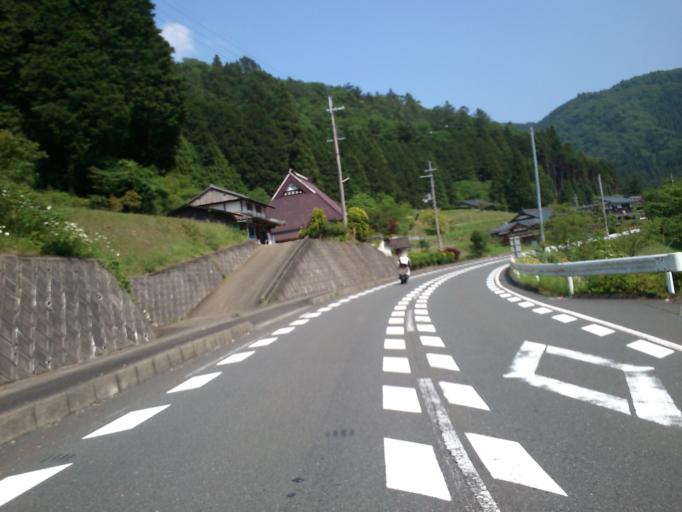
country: JP
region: Kyoto
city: Kameoka
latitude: 35.2336
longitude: 135.5697
